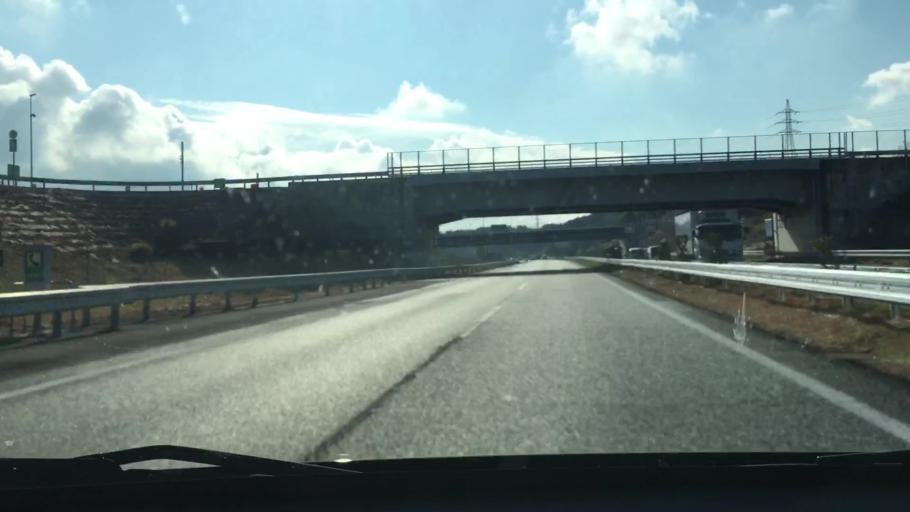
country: JP
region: Kumamoto
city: Matsubase
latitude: 32.5786
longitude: 130.7124
